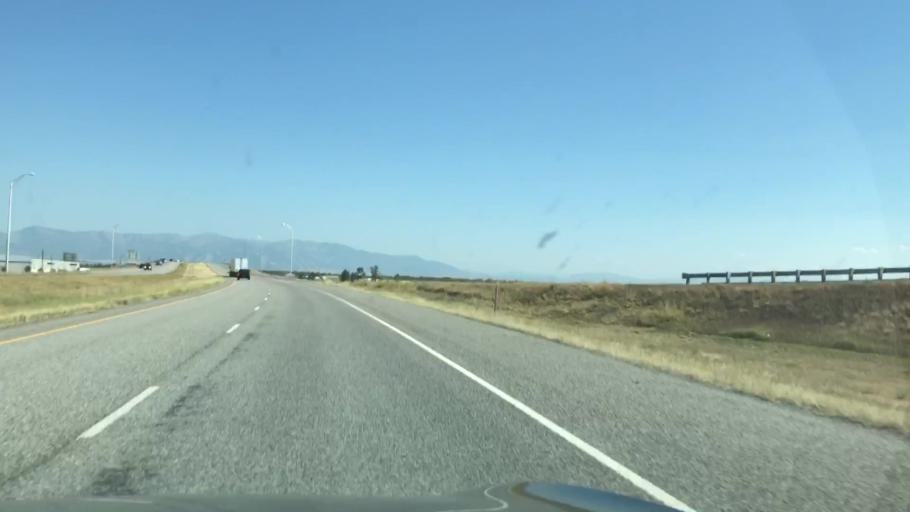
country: US
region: Montana
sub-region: Gallatin County
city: Manhattan
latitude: 45.8497
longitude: -111.3363
